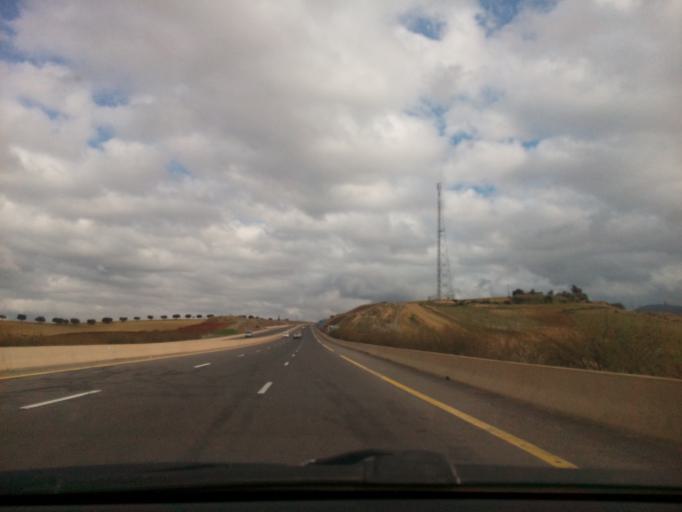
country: DZ
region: Tlemcen
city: Chetouane
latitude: 34.9832
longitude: -1.2383
